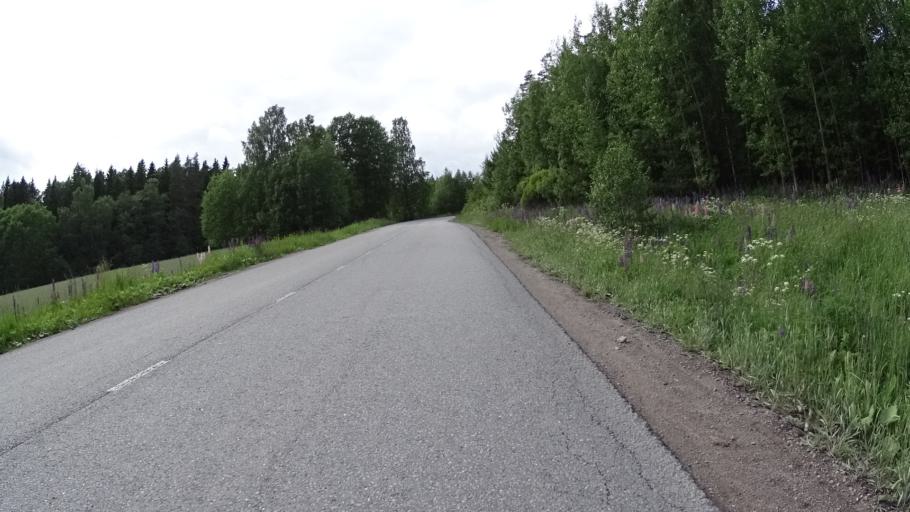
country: FI
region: Uusimaa
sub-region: Helsinki
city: Kilo
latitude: 60.2895
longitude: 24.8049
